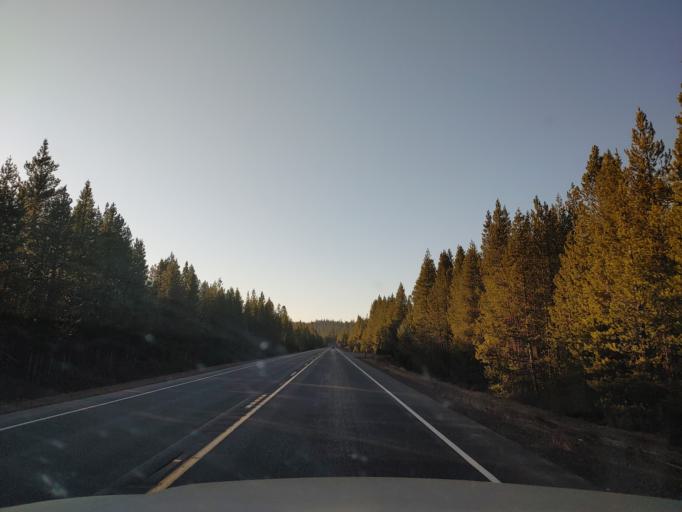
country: US
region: Oregon
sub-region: Deschutes County
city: La Pine
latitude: 43.4364
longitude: -121.8603
